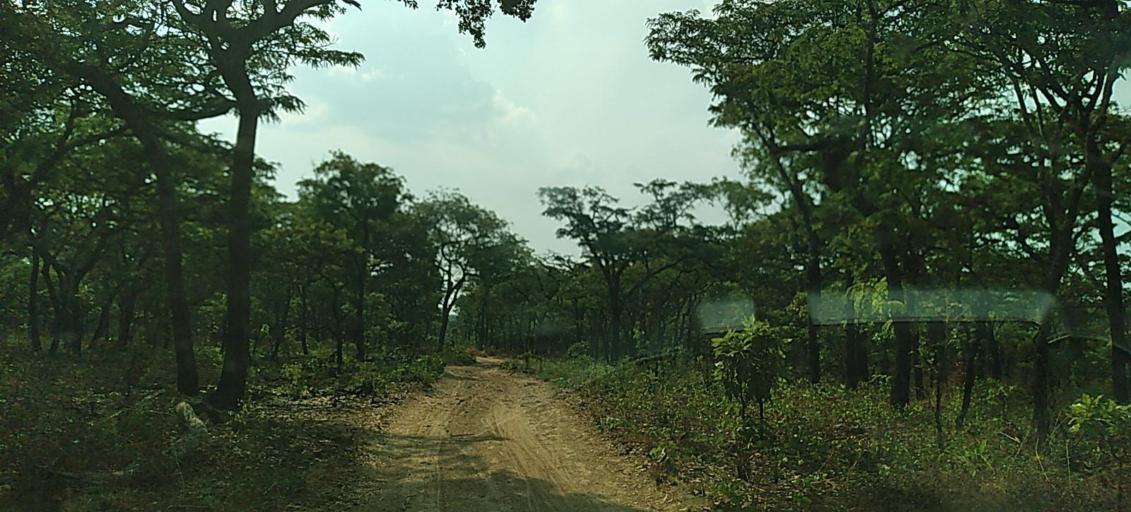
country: ZM
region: North-Western
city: Solwezi
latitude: -12.0709
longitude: 26.2271
